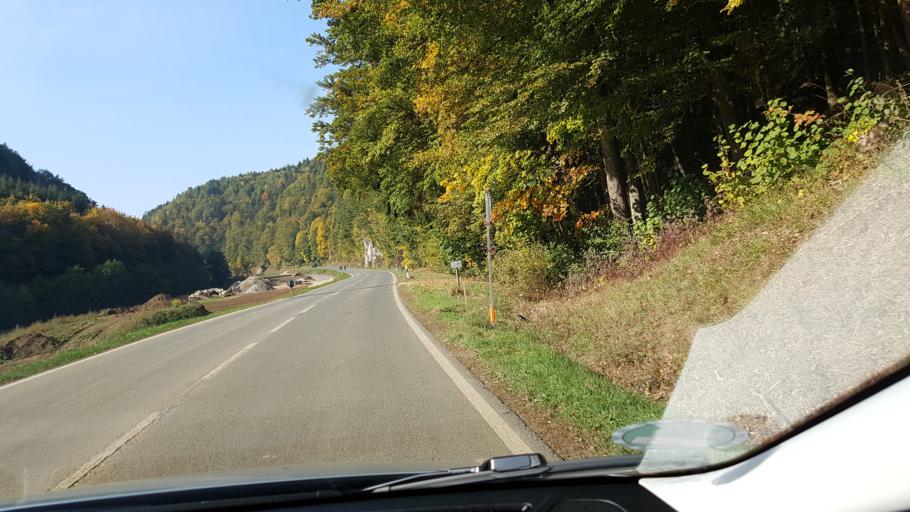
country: DE
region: Bavaria
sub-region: Upper Franconia
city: Waischenfeld
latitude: 49.8176
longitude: 11.3094
